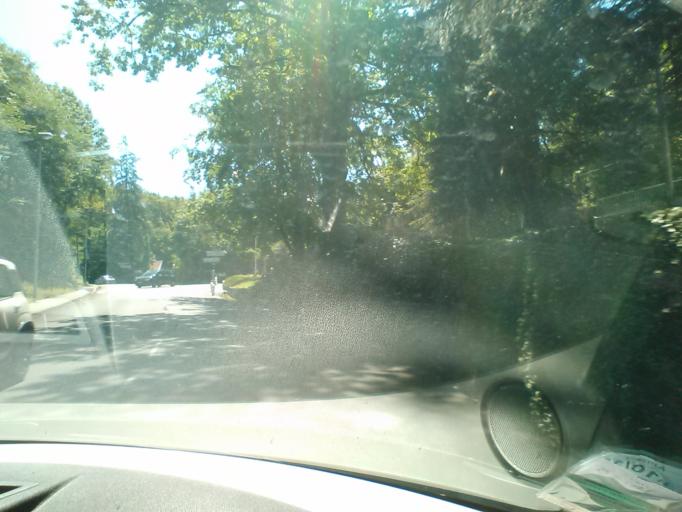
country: FR
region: Rhone-Alpes
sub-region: Departement de la Savoie
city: Chambery
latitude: 45.5614
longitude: 5.9307
